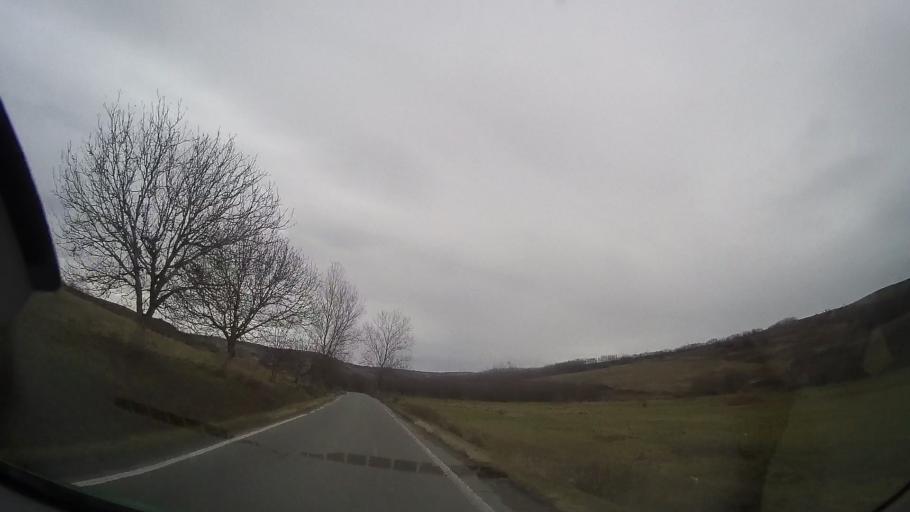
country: RO
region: Mures
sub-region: Comuna Bala
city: Bala
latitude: 46.7139
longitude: 24.5283
